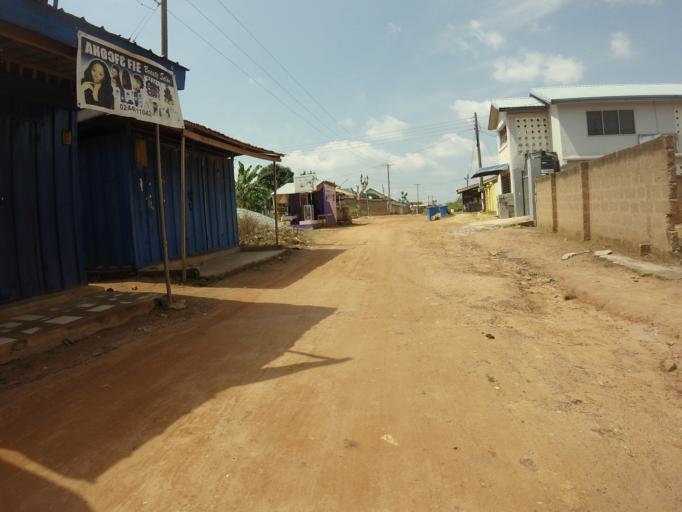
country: GH
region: Greater Accra
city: Gbawe
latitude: 5.6161
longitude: -0.3122
